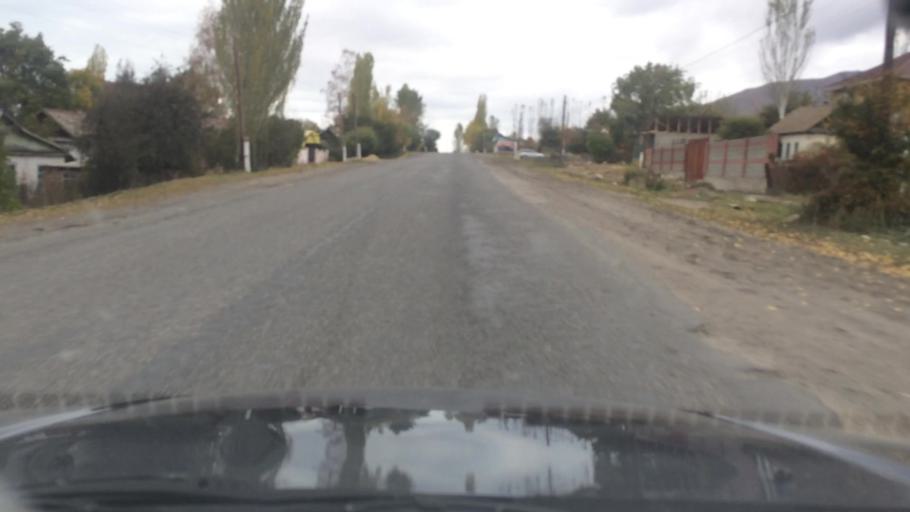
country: KG
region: Ysyk-Koel
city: Tyup
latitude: 42.7478
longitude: 78.1082
